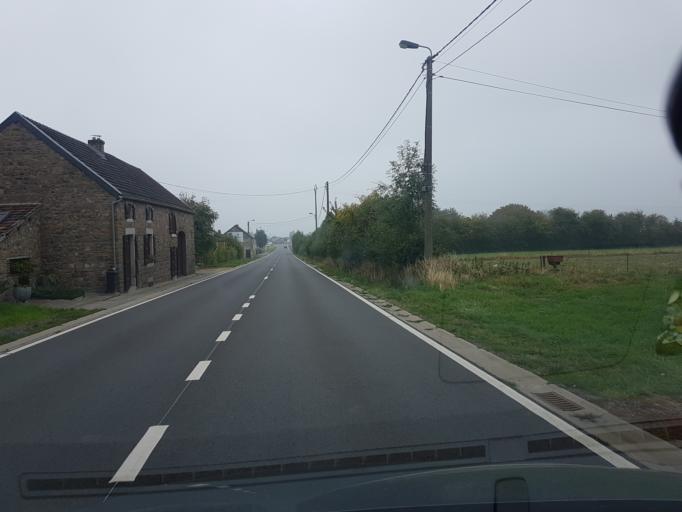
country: BE
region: Wallonia
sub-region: Province de Namur
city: Ohey
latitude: 50.4489
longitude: 5.1169
